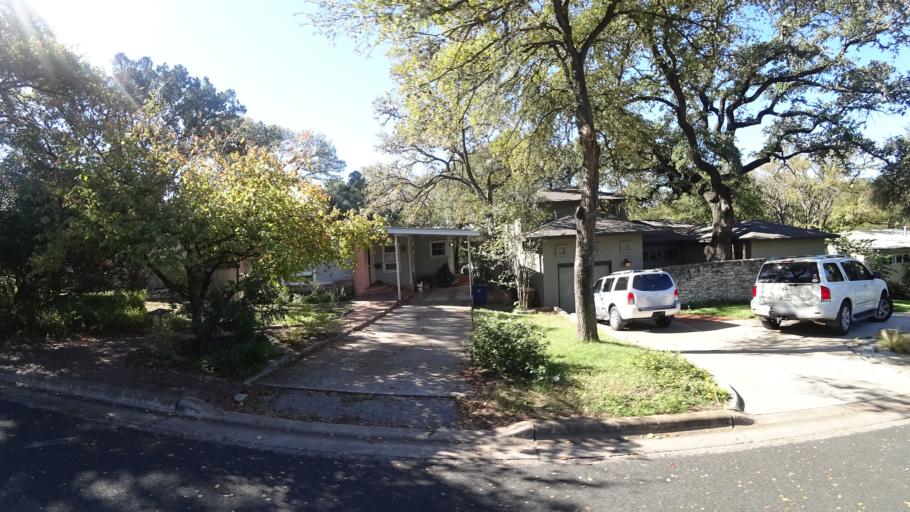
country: US
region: Texas
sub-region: Travis County
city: Rollingwood
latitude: 30.2827
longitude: -97.7689
